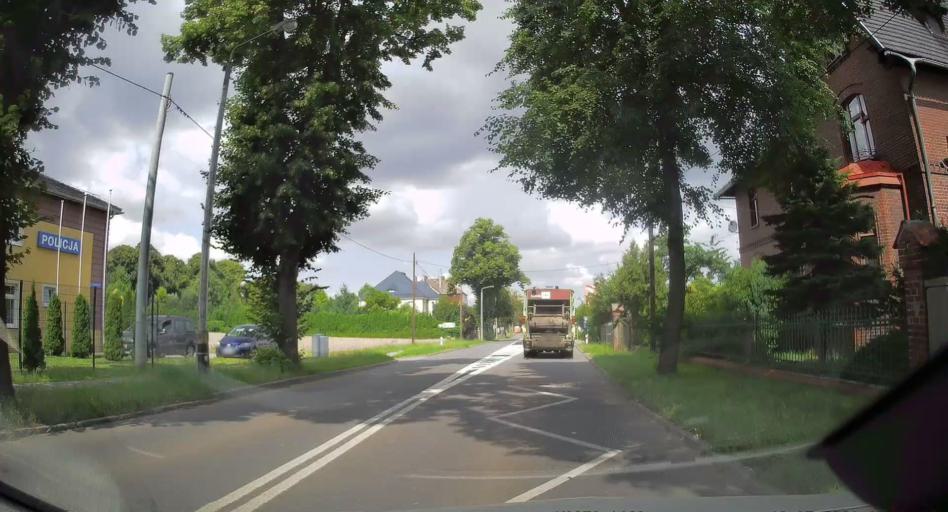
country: PL
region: Opole Voivodeship
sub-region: Powiat prudnicki
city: Glogowek
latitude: 50.3491
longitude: 17.8756
